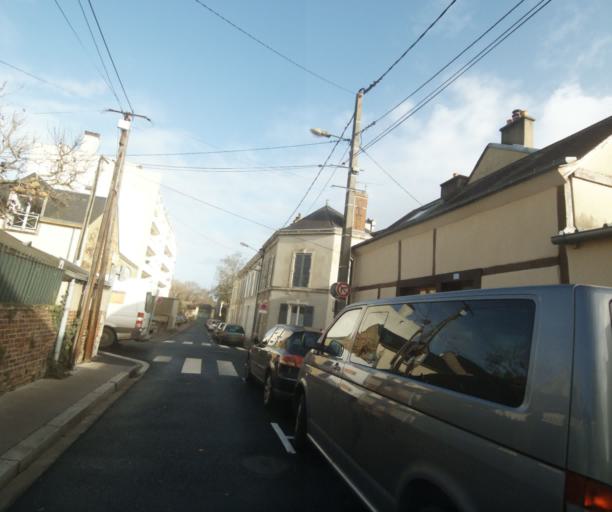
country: FR
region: Pays de la Loire
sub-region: Departement de la Sarthe
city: Le Mans
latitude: 47.9984
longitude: 0.1963
